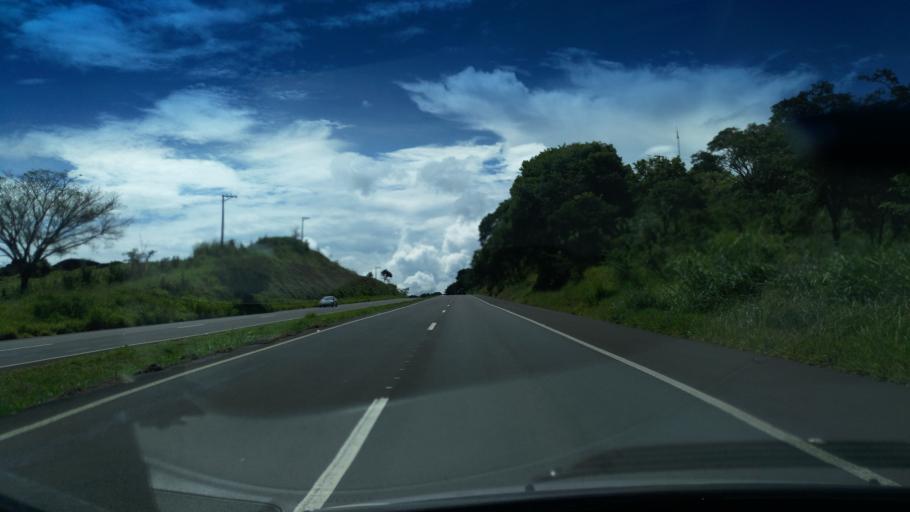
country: BR
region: Sao Paulo
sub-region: Santo Antonio Do Jardim
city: Espirito Santo do Pinhal
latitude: -22.1802
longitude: -46.7556
